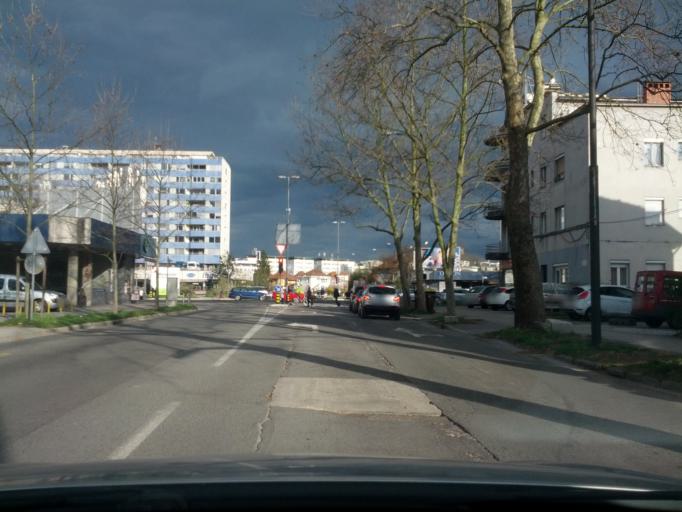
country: SI
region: Ljubljana
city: Ljubljana
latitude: 46.0638
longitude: 14.5074
